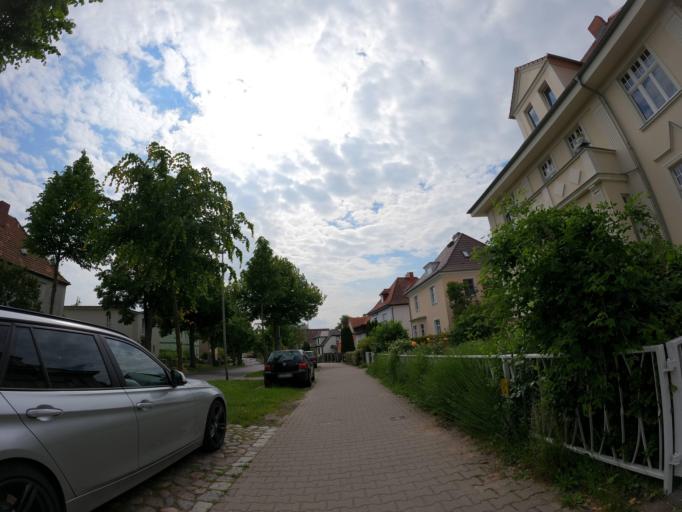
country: DE
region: Mecklenburg-Vorpommern
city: Stralsund
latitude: 54.3142
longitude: 13.0741
